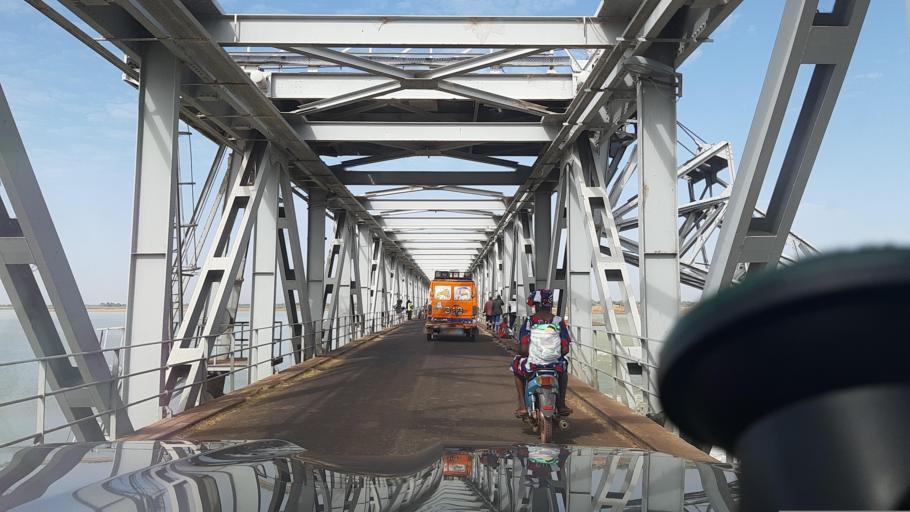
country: ML
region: Segou
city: Markala
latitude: 13.6791
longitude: -6.0780
